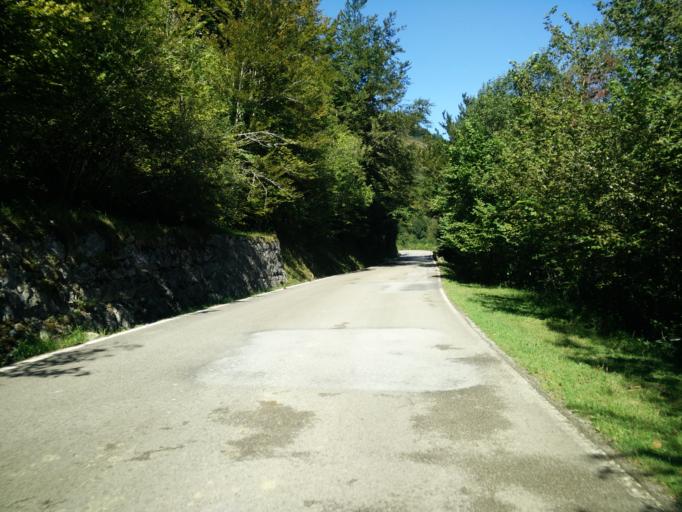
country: ES
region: Cantabria
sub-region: Provincia de Cantabria
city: Ruente
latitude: 43.1260
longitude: -4.2971
